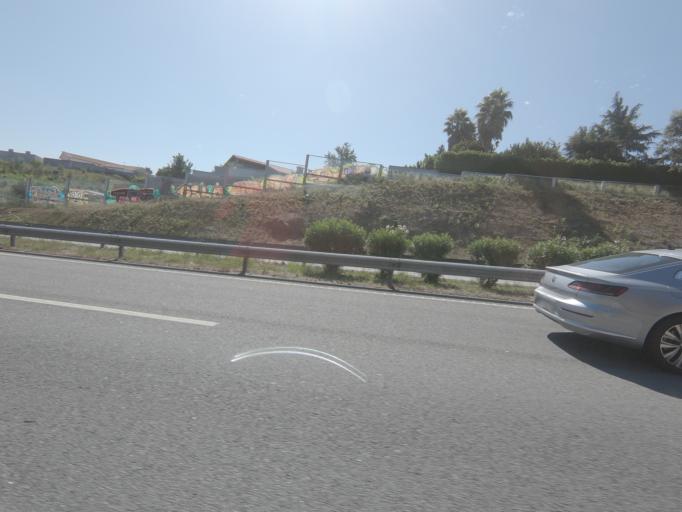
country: PT
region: Porto
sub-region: Paredes
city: Baltar
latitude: 41.1917
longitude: -8.3594
